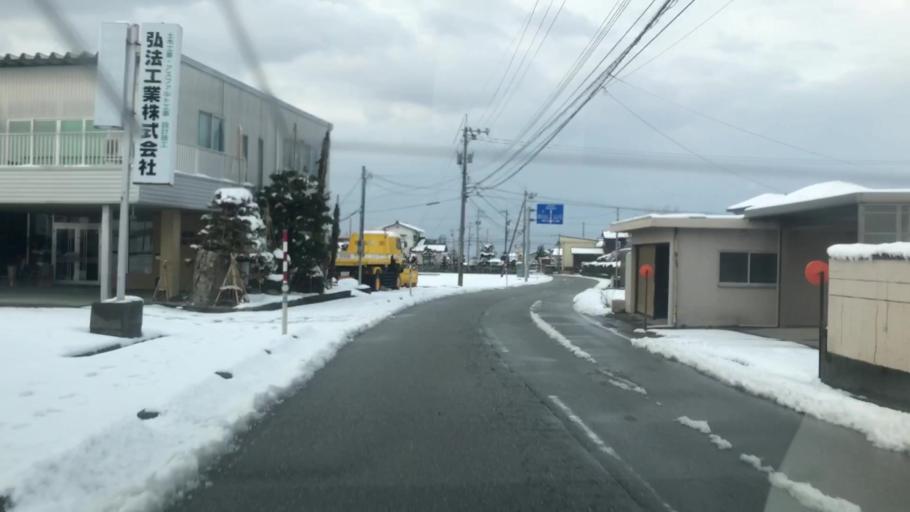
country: JP
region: Toyama
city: Toyama-shi
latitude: 36.6702
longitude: 137.2756
